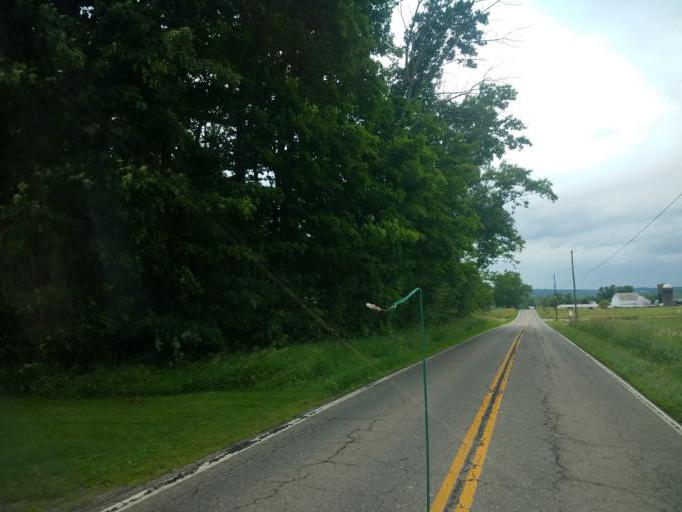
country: US
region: Ohio
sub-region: Columbiana County
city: Leetonia
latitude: 40.8525
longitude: -80.7723
